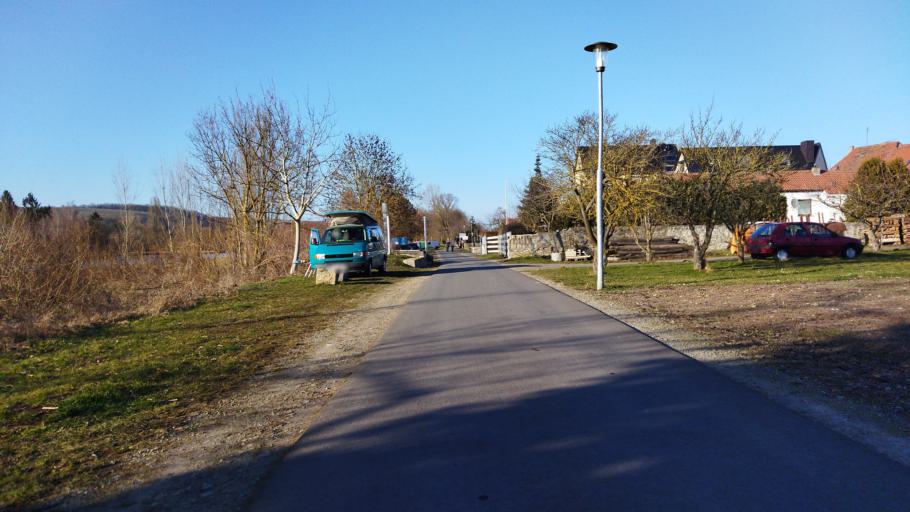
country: DE
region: Bavaria
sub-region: Regierungsbezirk Unterfranken
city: Albertshofen
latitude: 49.7706
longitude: 10.1577
